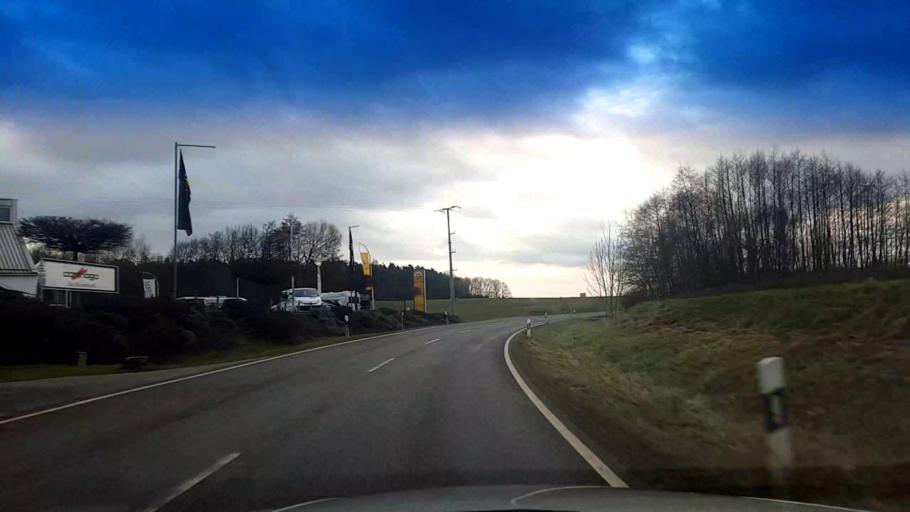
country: DE
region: Bavaria
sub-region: Upper Franconia
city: Litzendorf
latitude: 49.8672
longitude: 11.0255
